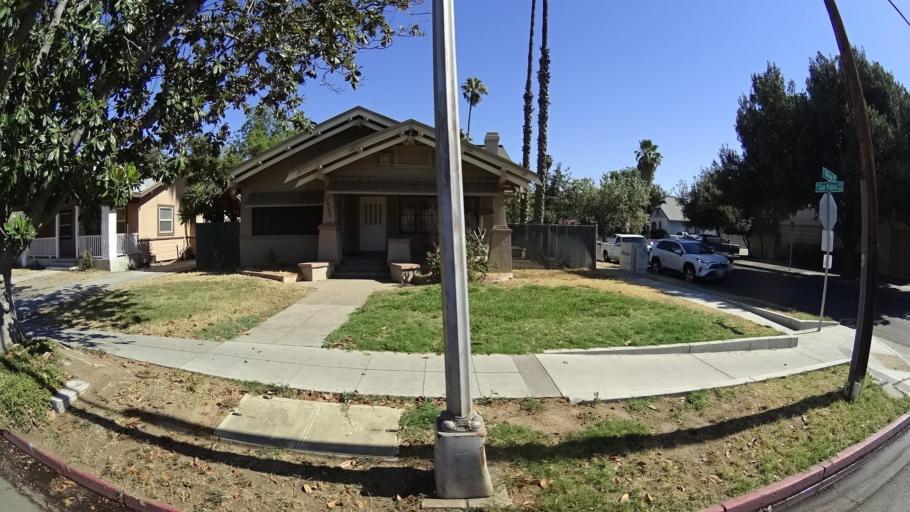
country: US
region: California
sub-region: Fresno County
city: Fresno
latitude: 36.7577
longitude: -119.7947
